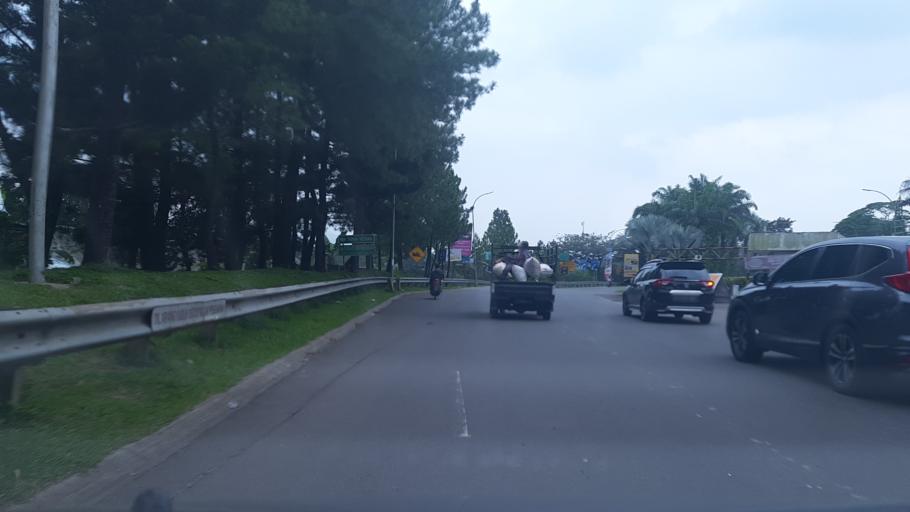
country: ID
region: West Java
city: Bogor
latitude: -6.5709
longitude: 106.8626
